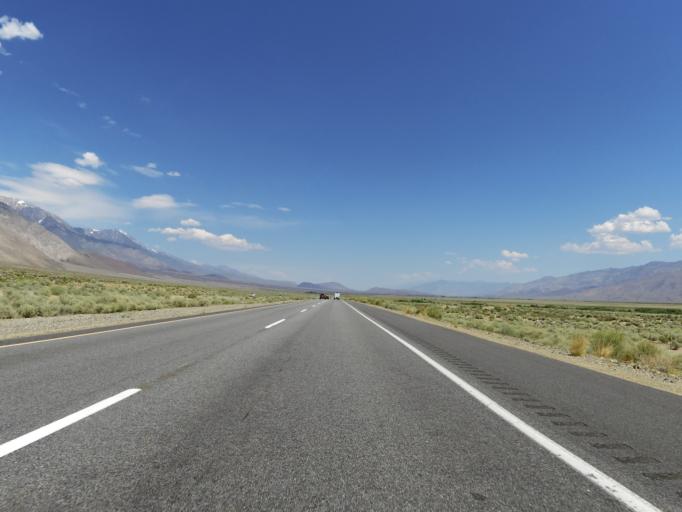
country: US
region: California
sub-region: Inyo County
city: Big Pine
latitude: 36.8641
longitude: -118.2353
